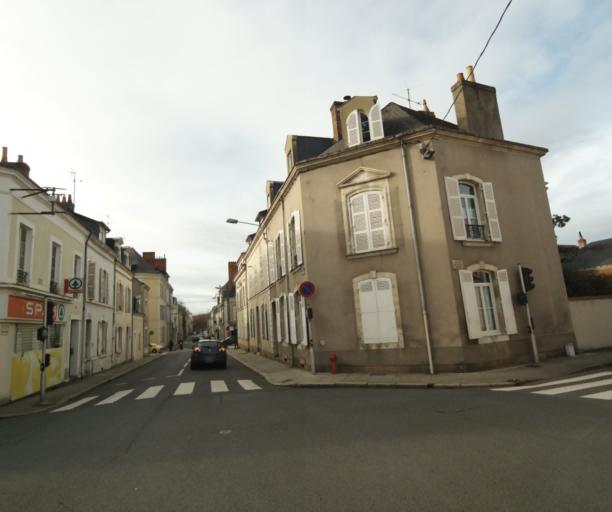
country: FR
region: Pays de la Loire
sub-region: Departement de la Sarthe
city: Le Mans
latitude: 48.0080
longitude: 0.2077
